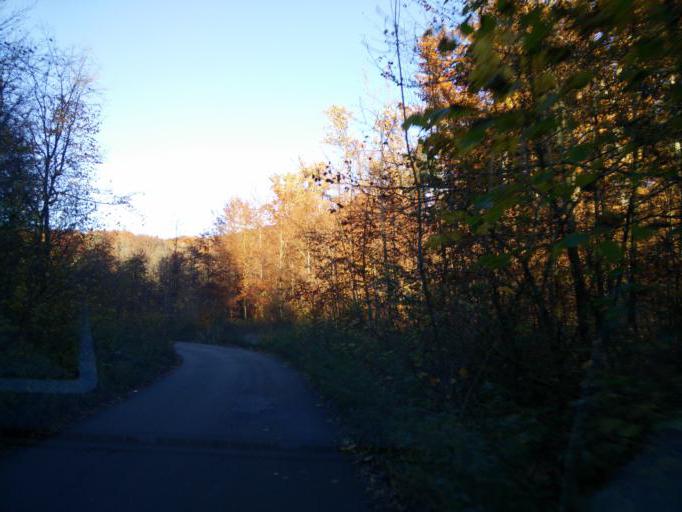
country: DE
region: Baden-Wuerttemberg
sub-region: Tuebingen Region
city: Gomaringen
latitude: 48.4340
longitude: 9.1117
